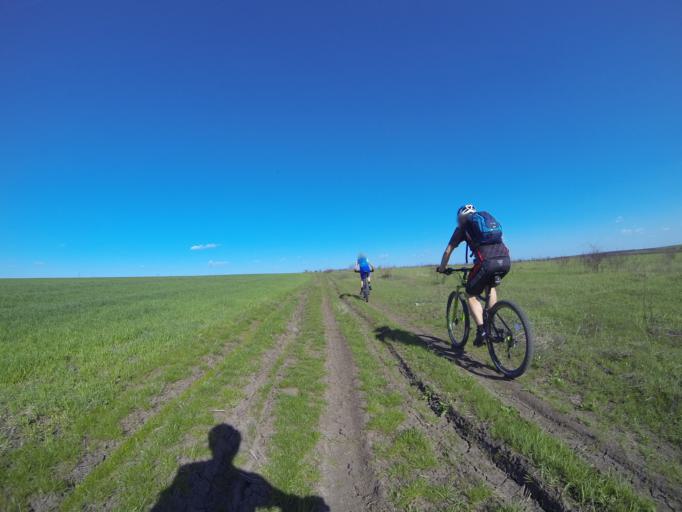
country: RO
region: Dolj
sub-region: Comuna Goesti
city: Goesti
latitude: 44.5099
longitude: 23.7832
